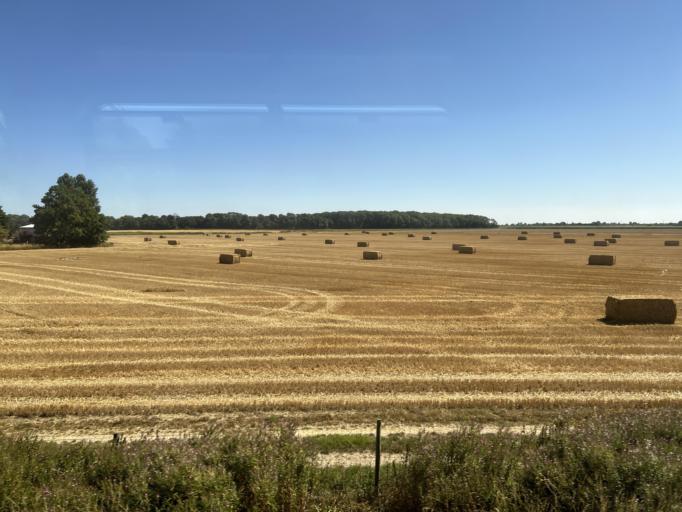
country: GB
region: England
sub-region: Lincolnshire
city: Spilsby
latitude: 53.1094
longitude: 0.1224
